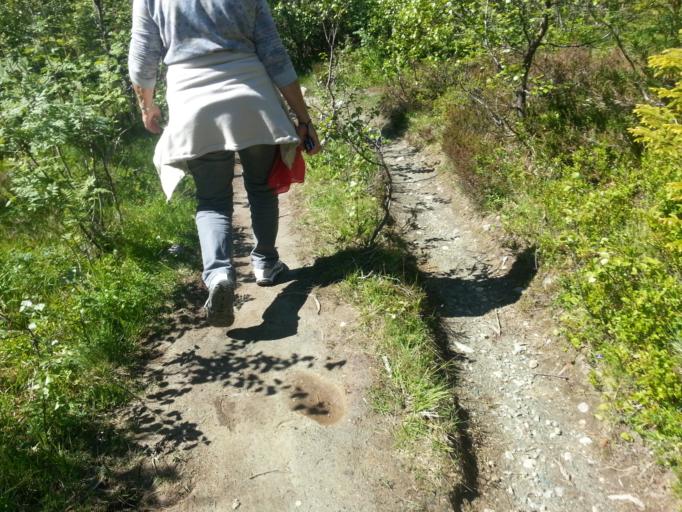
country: NO
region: Sor-Trondelag
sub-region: Trondheim
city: Trondheim
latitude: 63.4032
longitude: 10.2835
